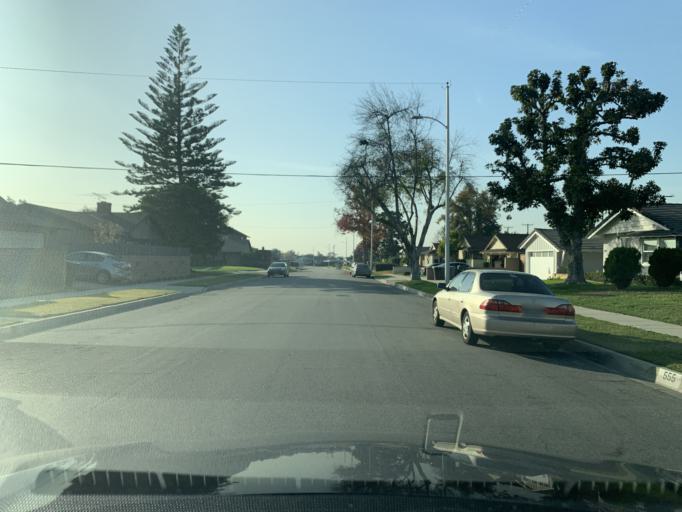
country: US
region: California
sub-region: Los Angeles County
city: Covina
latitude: 34.0917
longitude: -117.9003
